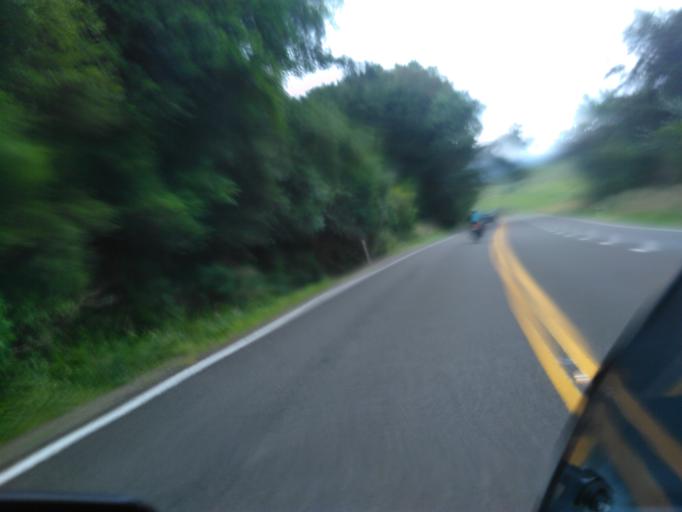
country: NZ
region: Bay of Plenty
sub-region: Opotiki District
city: Opotiki
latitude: -38.3962
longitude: 177.5611
